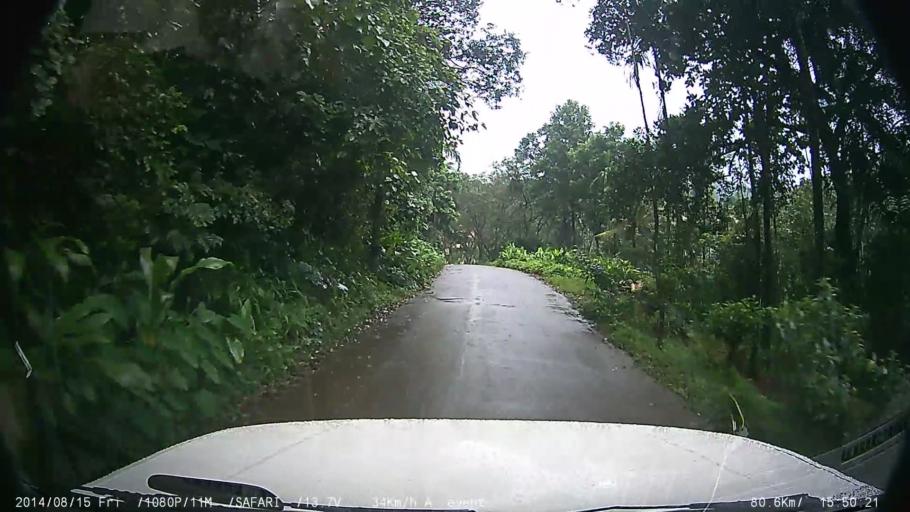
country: IN
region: Kerala
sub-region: Kottayam
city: Lalam
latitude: 9.8071
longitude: 76.7298
